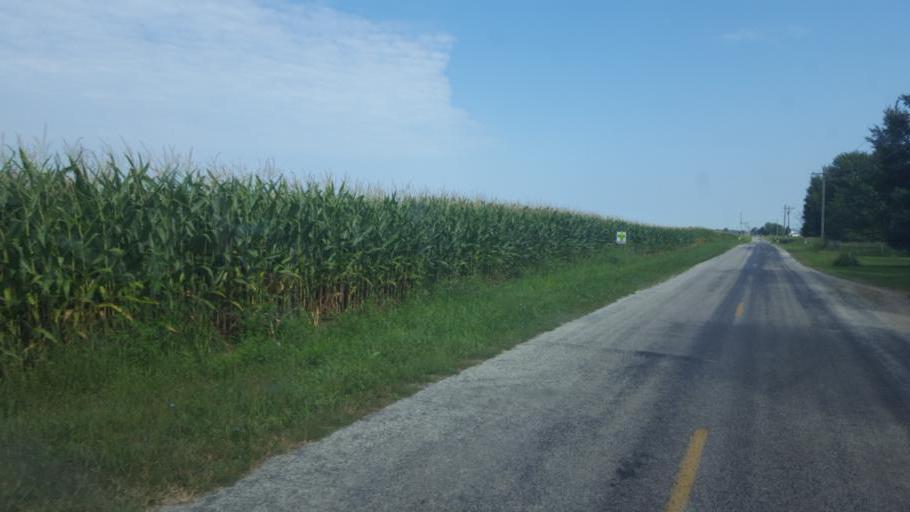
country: US
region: Ohio
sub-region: Morrow County
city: Cardington
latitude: 40.5037
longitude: -82.9956
